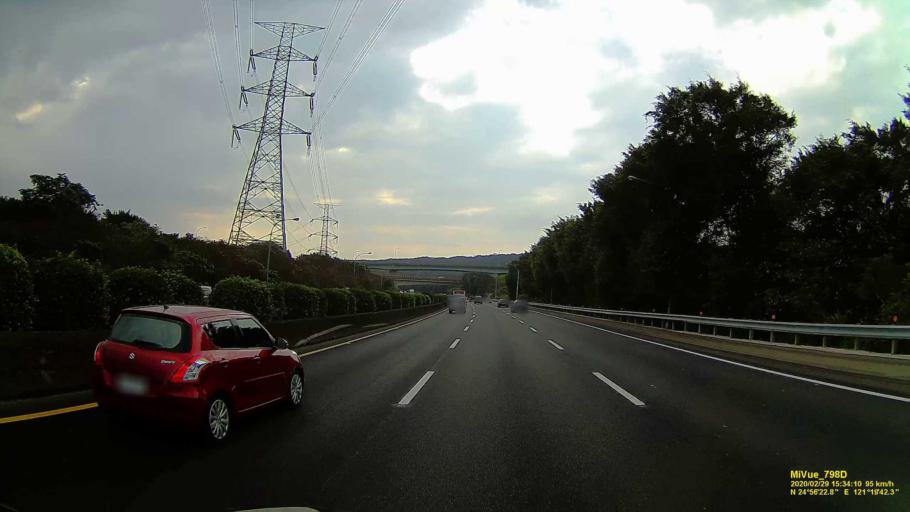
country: TW
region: Taiwan
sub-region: Taoyuan
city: Taoyuan
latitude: 24.9399
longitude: 121.3280
